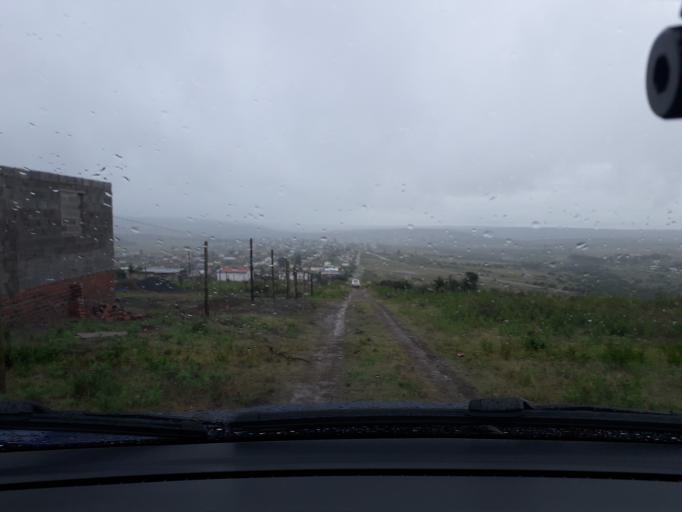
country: ZA
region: Eastern Cape
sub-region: Buffalo City Metropolitan Municipality
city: Bhisho
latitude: -32.8033
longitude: 27.3629
